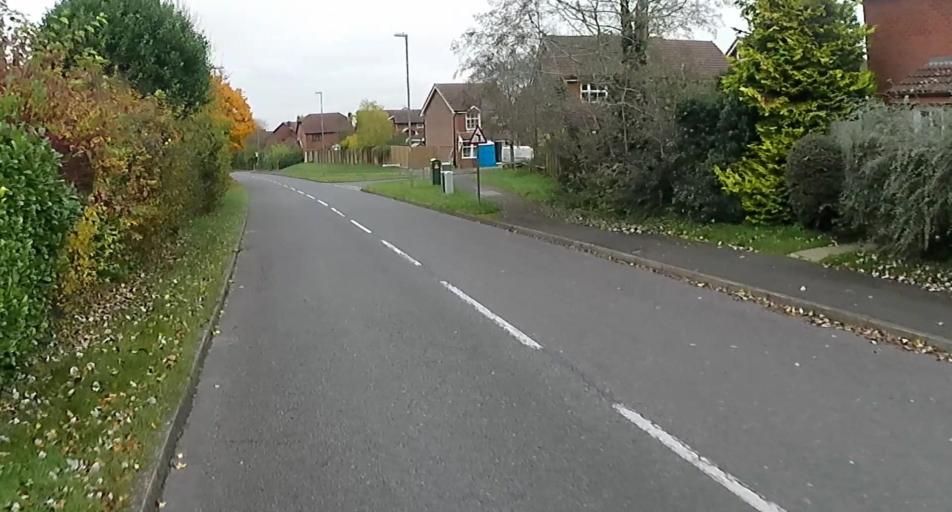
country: GB
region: England
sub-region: Hampshire
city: Basingstoke
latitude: 51.2367
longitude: -1.1362
